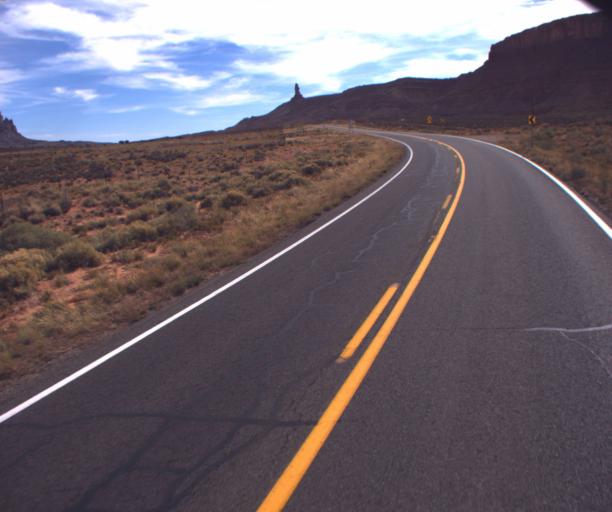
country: US
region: Arizona
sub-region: Navajo County
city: Kayenta
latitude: 36.8486
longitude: -110.2708
